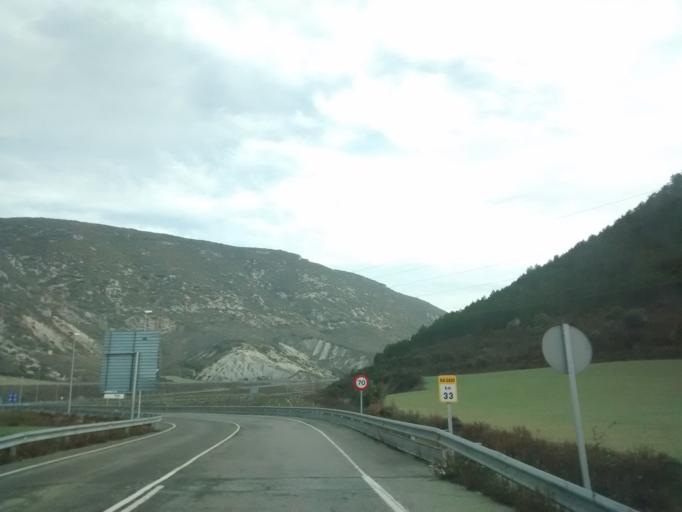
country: ES
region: Navarre
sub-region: Provincia de Navarra
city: Liedena
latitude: 42.6212
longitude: -1.2707
